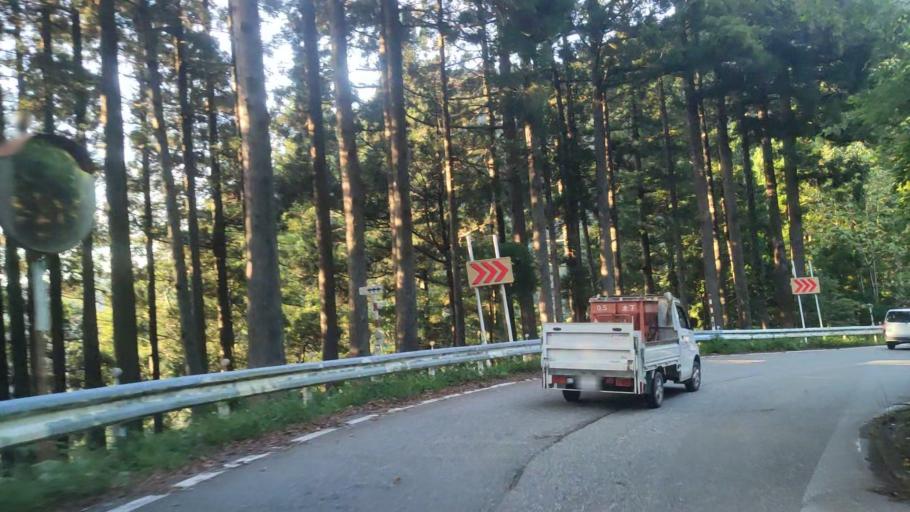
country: JP
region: Toyama
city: Nanto-shi
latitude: 36.5559
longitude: 137.0109
